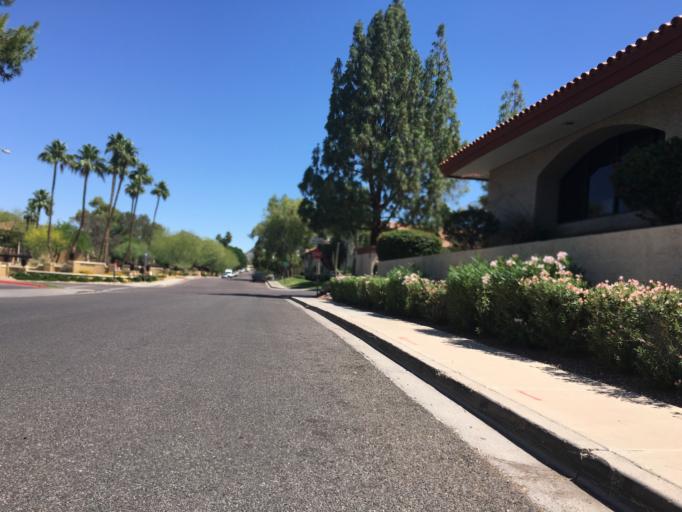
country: US
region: Arizona
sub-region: Maricopa County
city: Paradise Valley
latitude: 33.5453
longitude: -112.0429
